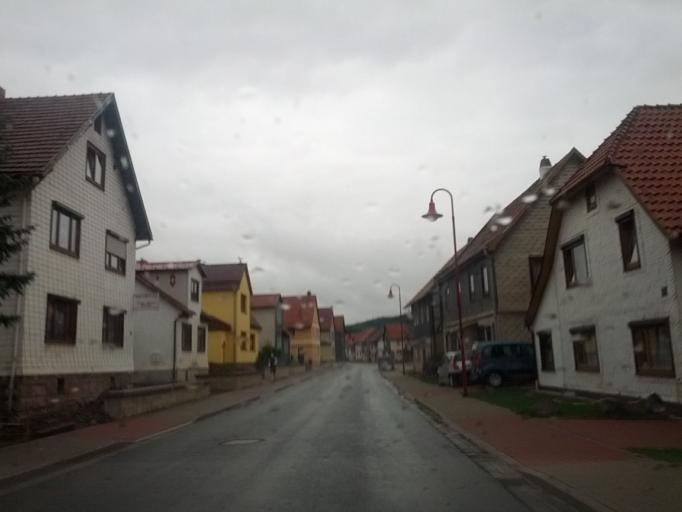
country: DE
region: Thuringia
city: Tabarz
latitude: 50.9017
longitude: 10.4753
